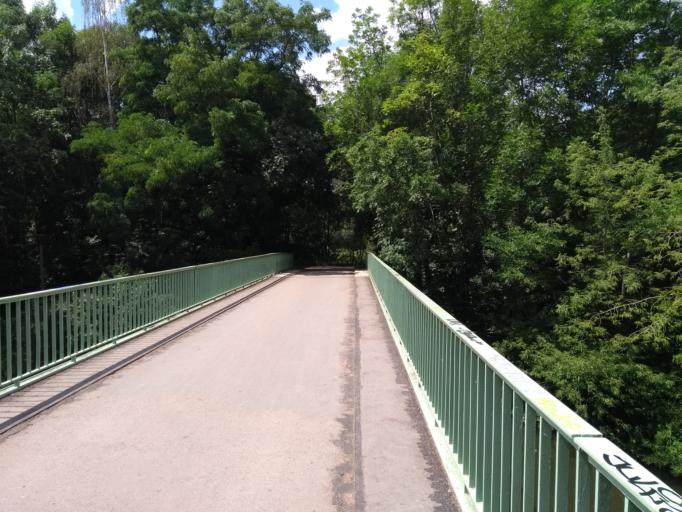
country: DE
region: Saxony-Anhalt
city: Halle Neustadt
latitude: 51.4656
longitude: 11.9485
